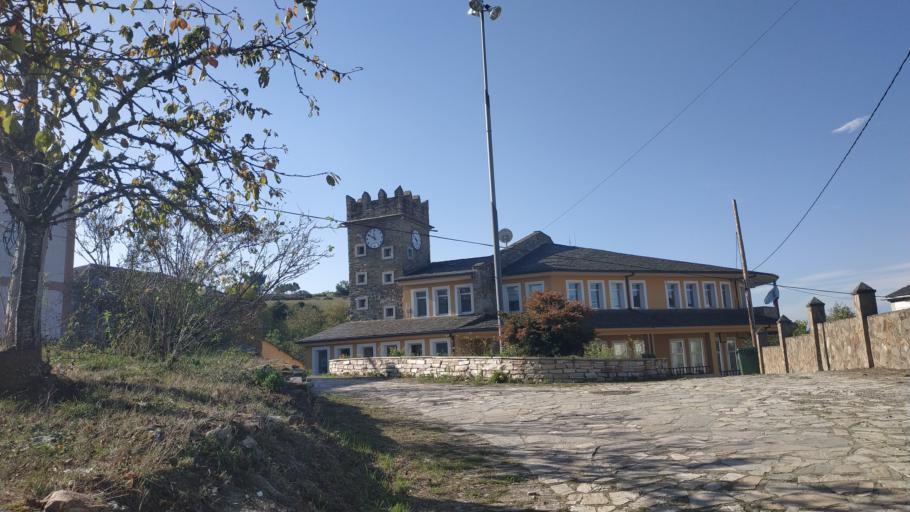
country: ES
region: Galicia
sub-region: Provincia de Lugo
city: San Roman
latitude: 42.8732
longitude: -7.0630
